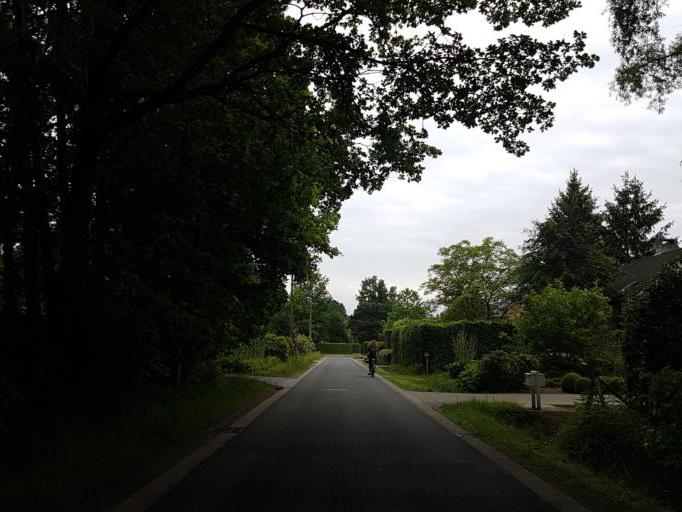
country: BE
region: Flanders
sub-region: Provincie Antwerpen
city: Zoersel
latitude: 51.2878
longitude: 4.6834
